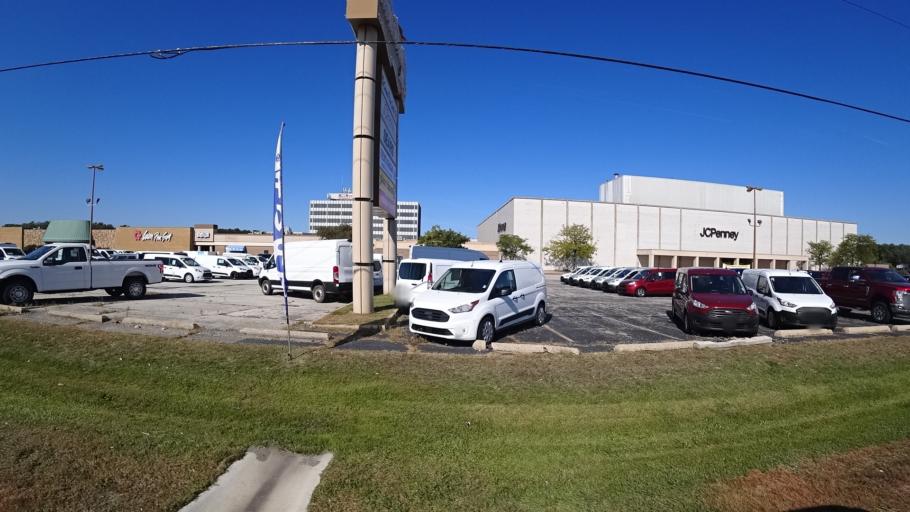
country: US
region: Indiana
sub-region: LaPorte County
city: Michigan City
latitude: 41.6805
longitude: -86.8968
